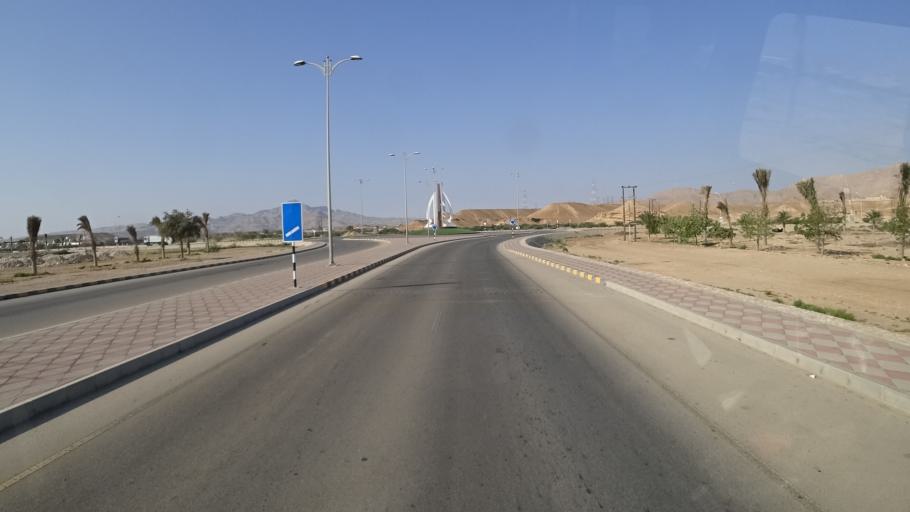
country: OM
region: Ash Sharqiyah
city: Sur
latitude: 22.5754
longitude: 59.4668
